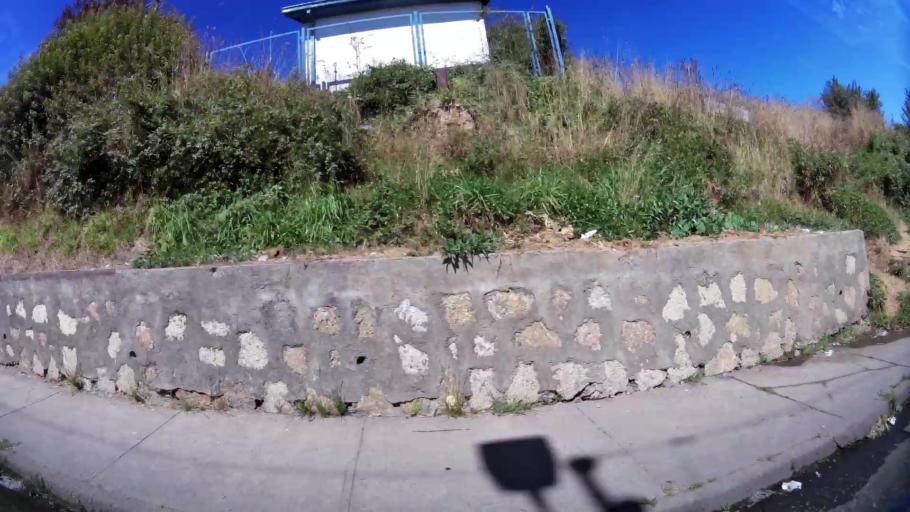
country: CL
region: Biobio
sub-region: Provincia de Concepcion
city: Penco
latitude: -36.7291
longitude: -72.9874
